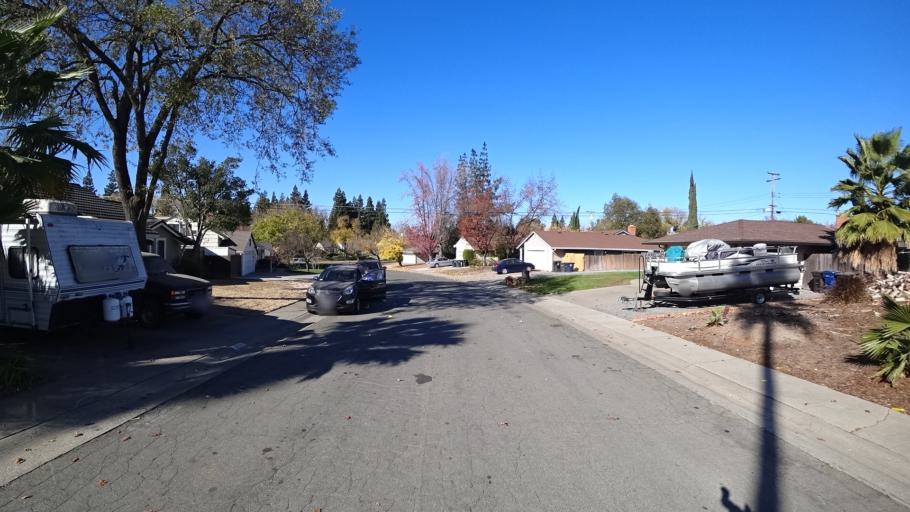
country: US
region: California
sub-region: Sacramento County
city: Foothill Farms
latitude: 38.6760
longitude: -121.3184
